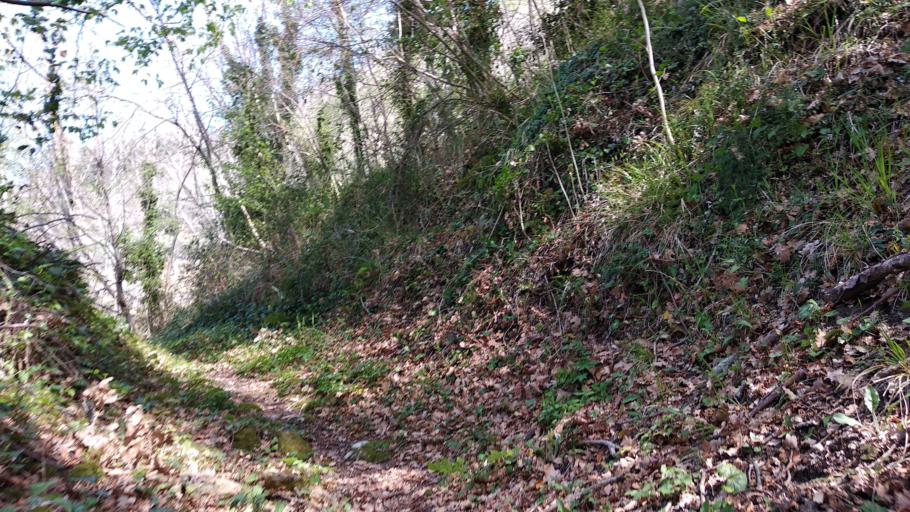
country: IT
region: Calabria
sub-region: Provincia di Cosenza
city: Altilia
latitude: 39.1275
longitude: 16.2488
